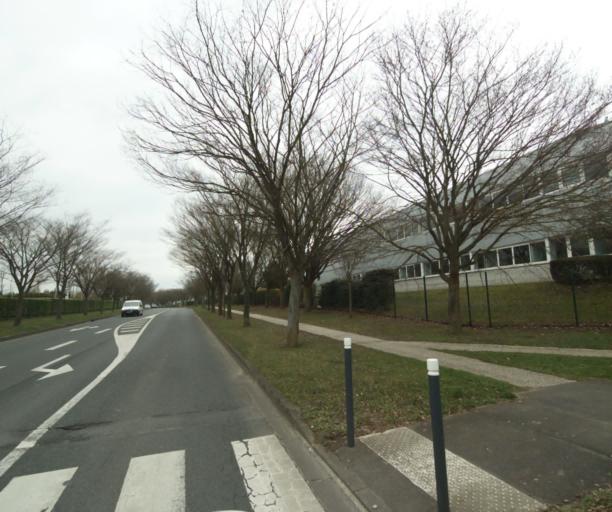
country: FR
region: Ile-de-France
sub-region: Departement du Val-d'Oise
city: Osny
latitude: 49.0547
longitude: 2.0411
